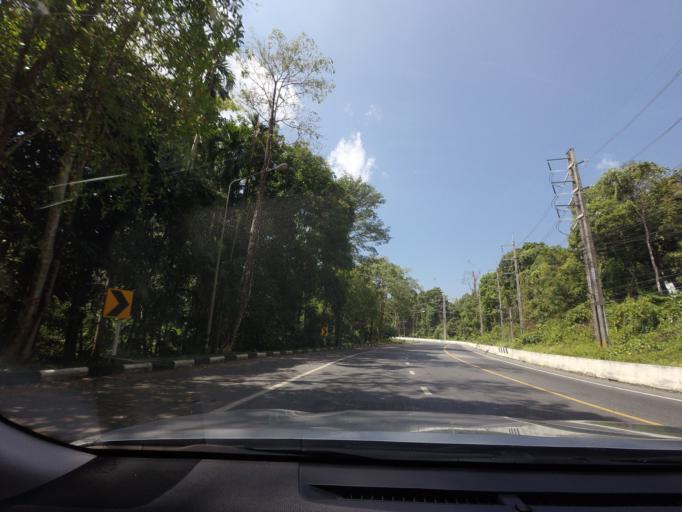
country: TH
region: Phangnga
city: Ban Khao Lak
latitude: 8.6229
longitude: 98.2375
